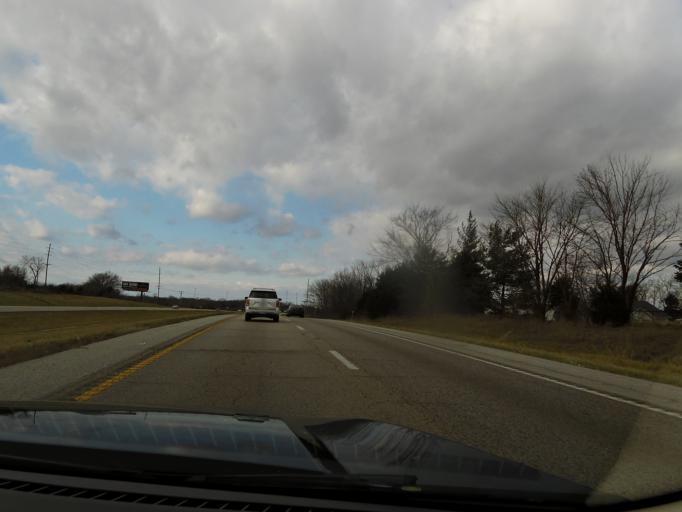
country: US
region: Missouri
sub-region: Lincoln County
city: Moscow Mills
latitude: 38.8746
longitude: -90.9046
